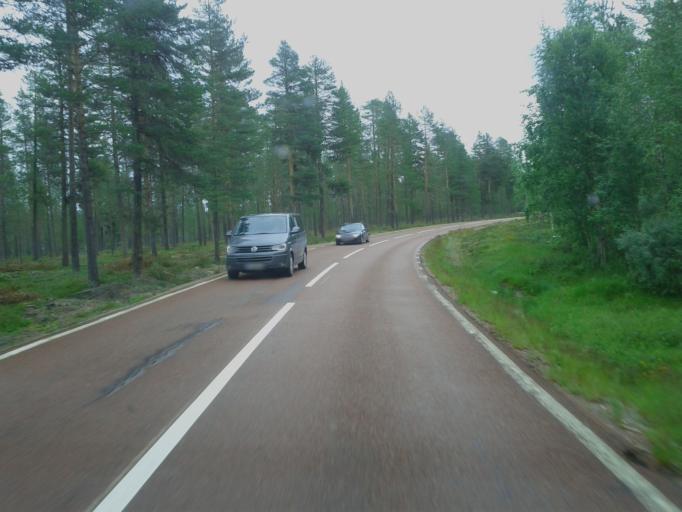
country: NO
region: Hedmark
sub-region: Trysil
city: Innbygda
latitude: 61.8525
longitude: 12.6871
